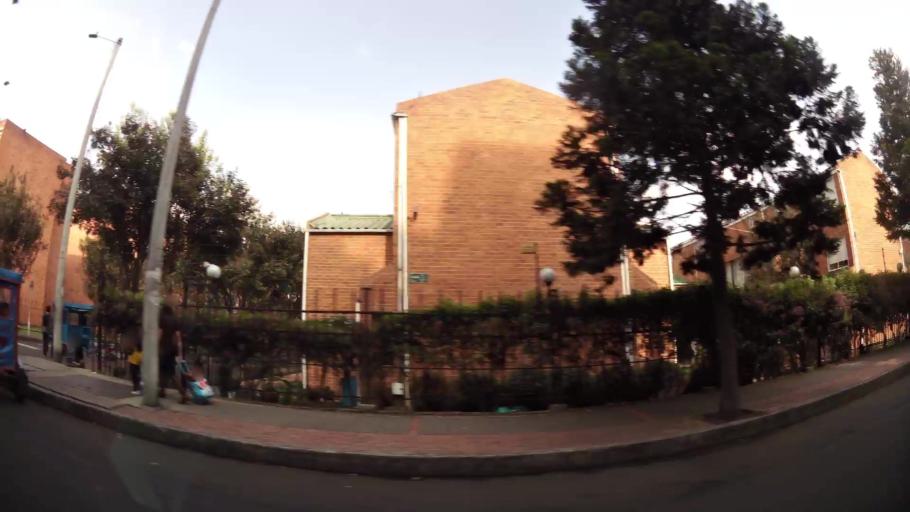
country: CO
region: Bogota D.C.
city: Barrio San Luis
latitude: 4.7377
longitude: -74.0576
